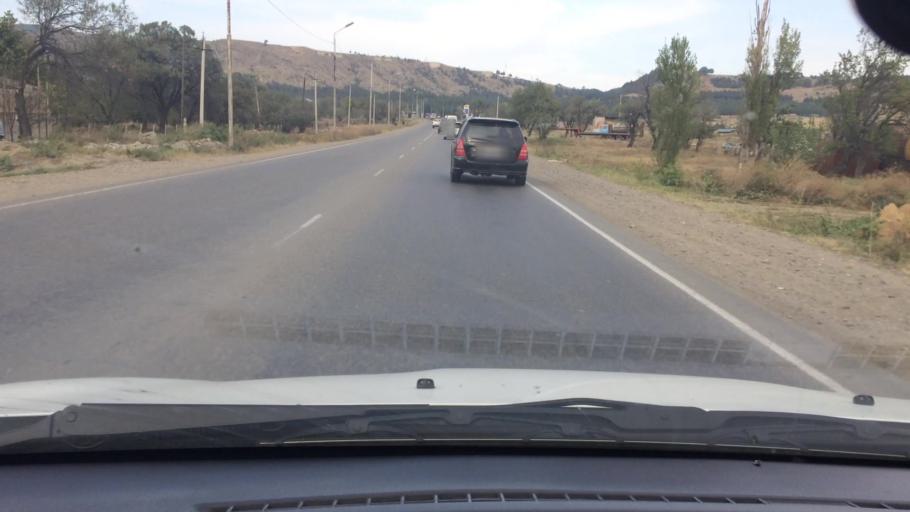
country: GE
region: T'bilisi
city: Tbilisi
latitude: 41.6150
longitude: 44.7907
